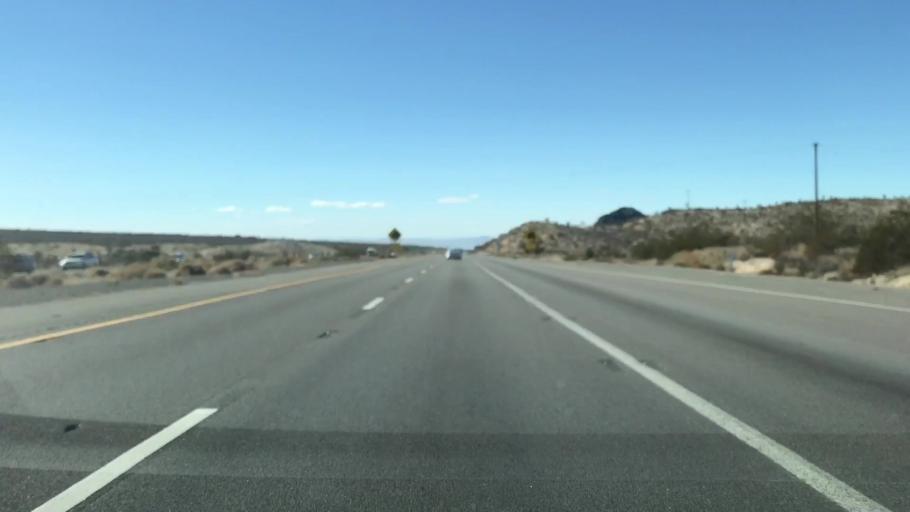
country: US
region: Nevada
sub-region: Clark County
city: Sandy Valley
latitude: 35.4017
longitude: -115.7957
